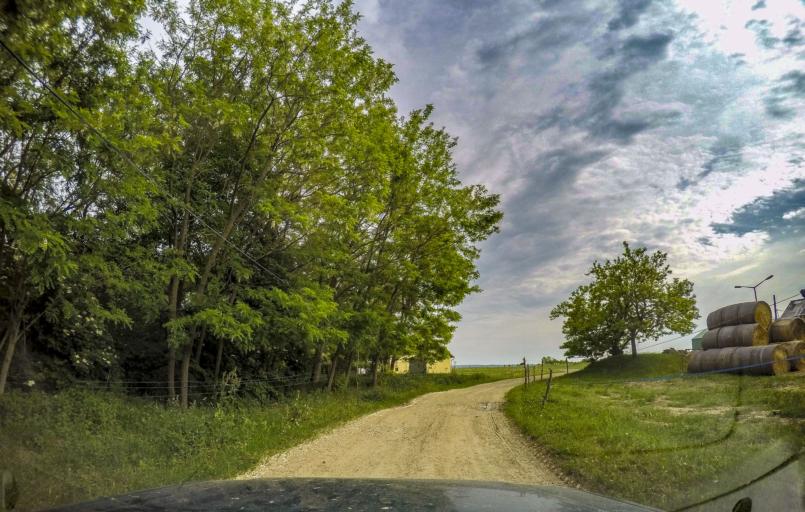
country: HU
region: Somogy
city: Karad
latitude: 46.7471
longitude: 17.8711
